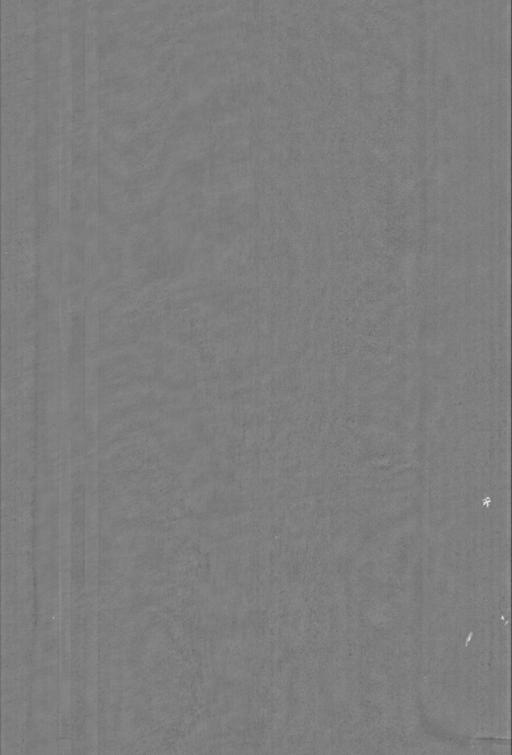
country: US
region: Washington, D.C.
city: Washington, D.C.
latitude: 38.8888
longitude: -76.9878
